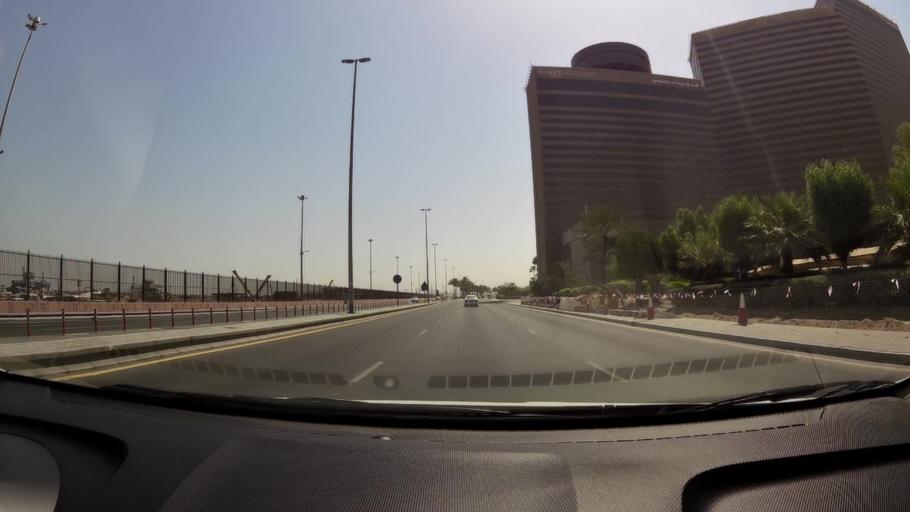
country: AE
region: Ash Shariqah
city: Sharjah
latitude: 25.2791
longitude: 55.3032
